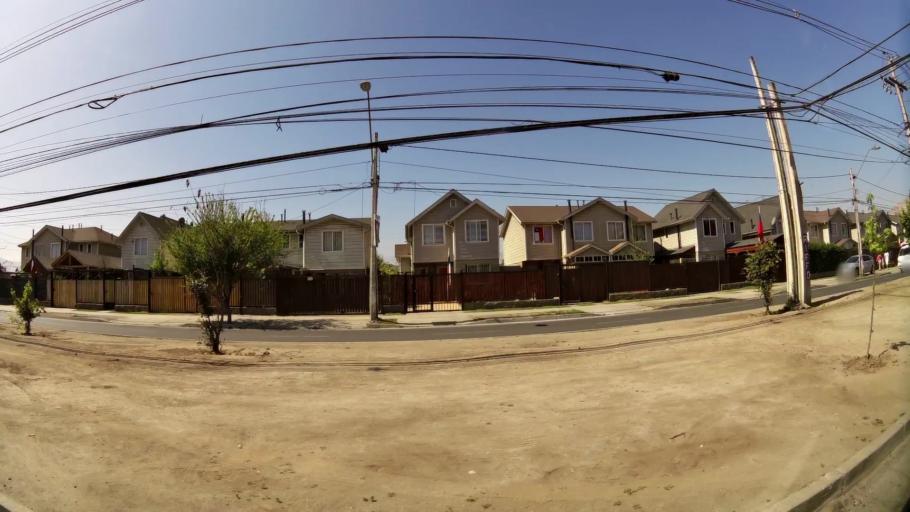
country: CL
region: Santiago Metropolitan
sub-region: Provincia de Santiago
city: Lo Prado
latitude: -33.3624
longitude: -70.7210
